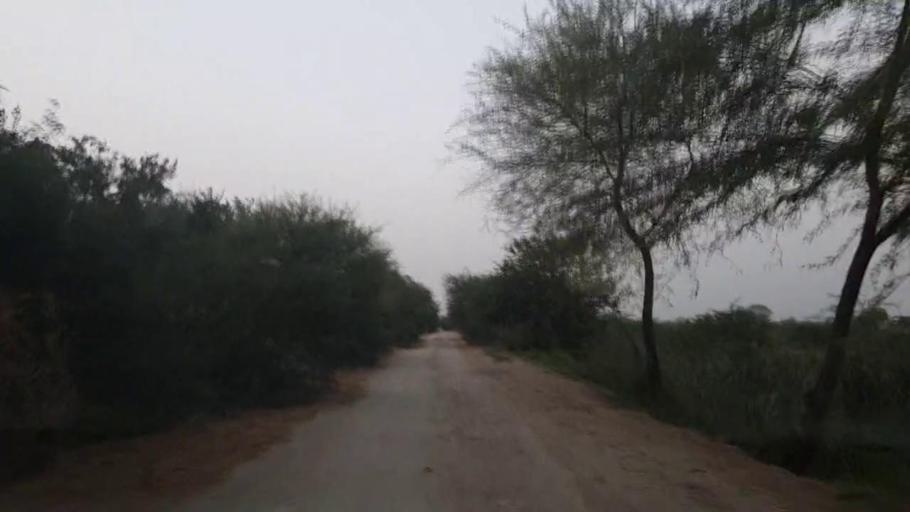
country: PK
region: Sindh
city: Mirpur Sakro
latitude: 24.5837
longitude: 67.7846
